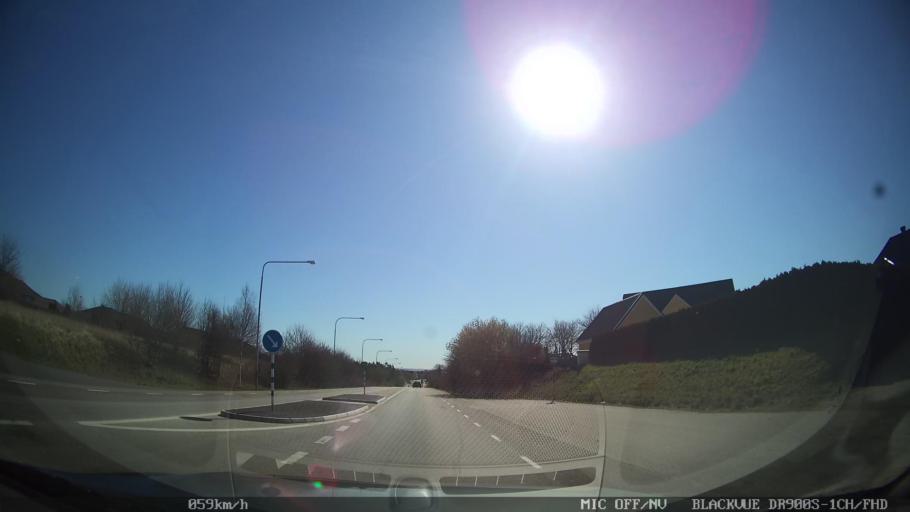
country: SE
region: Skane
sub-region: Ystads Kommun
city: Ystad
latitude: 55.4363
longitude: 13.7961
